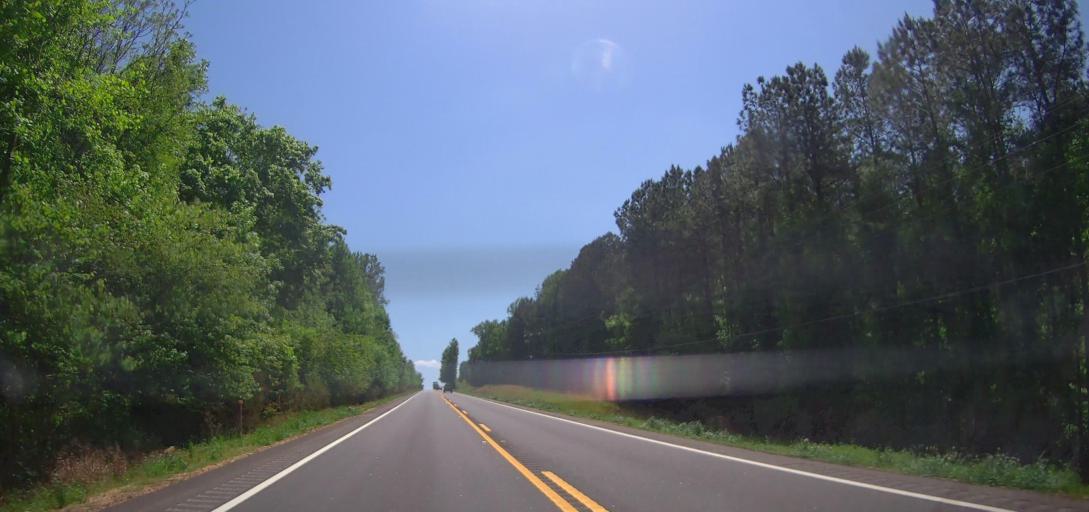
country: US
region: Georgia
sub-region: Putnam County
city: Eatonton
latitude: 33.2460
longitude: -83.4305
